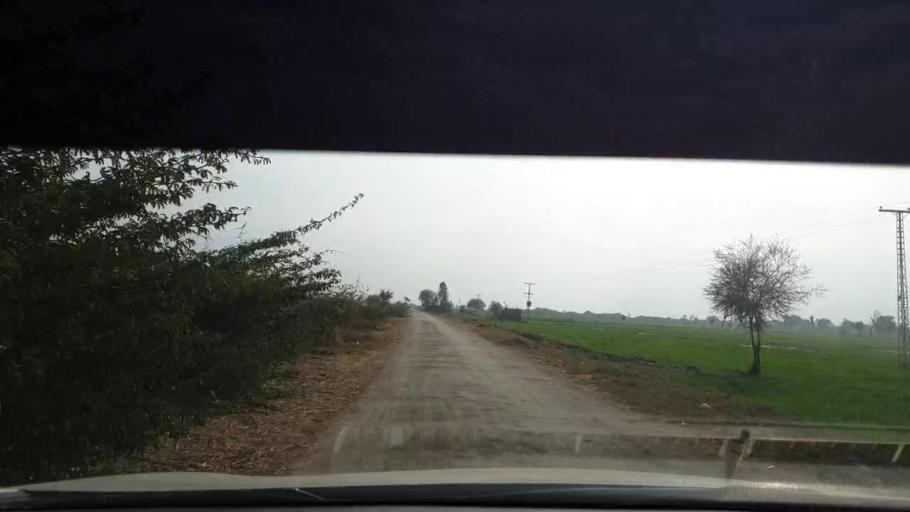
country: PK
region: Sindh
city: Berani
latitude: 25.7709
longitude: 68.8761
